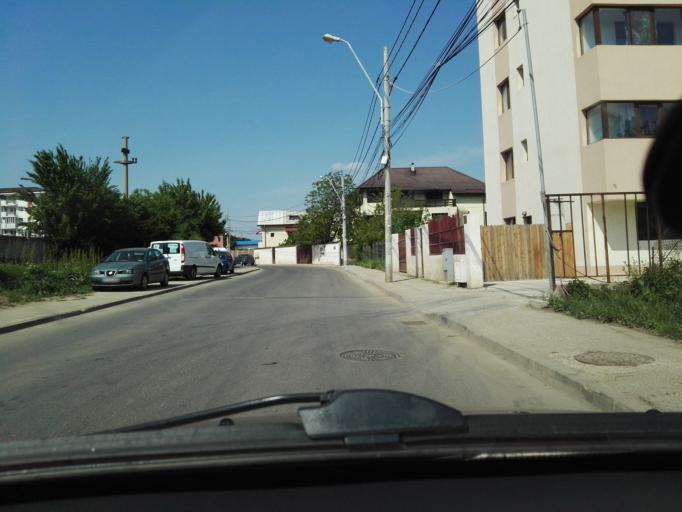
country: RO
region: Ilfov
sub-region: Comuna Popesti-Leordeni
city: Popesti-Leordeni
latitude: 44.3716
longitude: 26.1287
